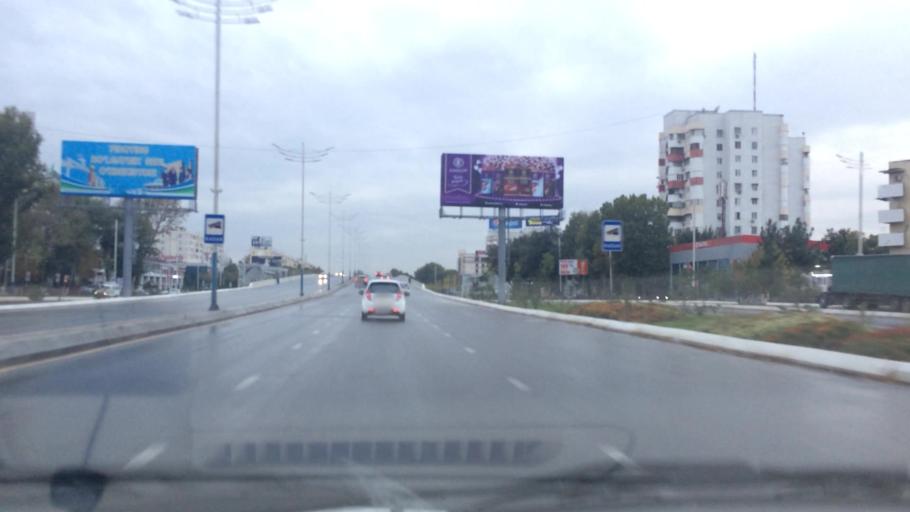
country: UZ
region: Toshkent Shahri
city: Tashkent
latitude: 41.2945
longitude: 69.2260
